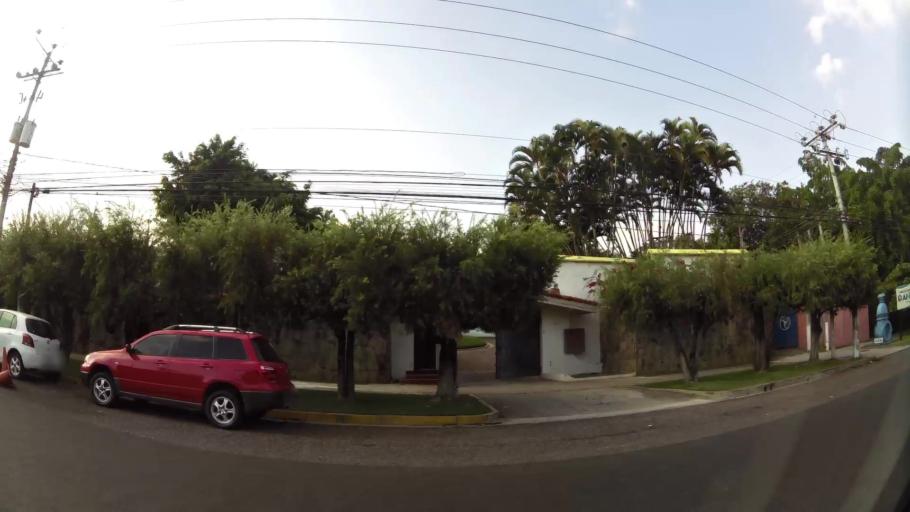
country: SV
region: La Libertad
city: Antiguo Cuscatlan
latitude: 13.6945
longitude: -89.2435
